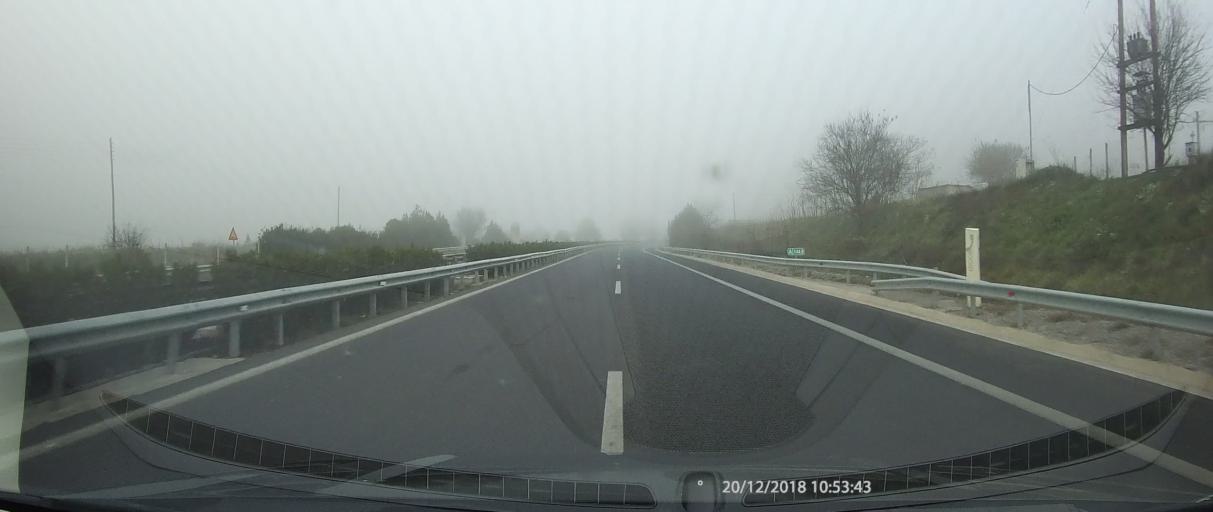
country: GR
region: Peloponnese
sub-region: Nomos Arkadias
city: Tripoli
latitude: 37.6134
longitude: 22.4578
